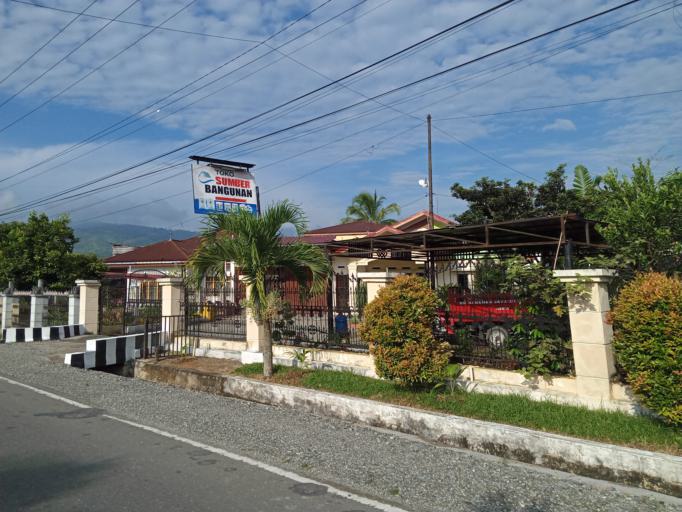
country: ID
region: Jambi
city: Semurup
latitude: -2.0009
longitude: 101.3771
